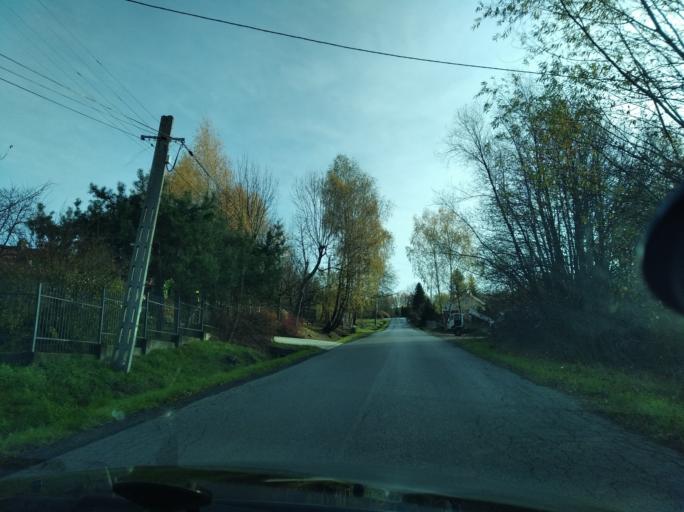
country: PL
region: Subcarpathian Voivodeship
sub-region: Powiat rzeszowski
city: Tyczyn
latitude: 49.9940
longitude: 22.0627
